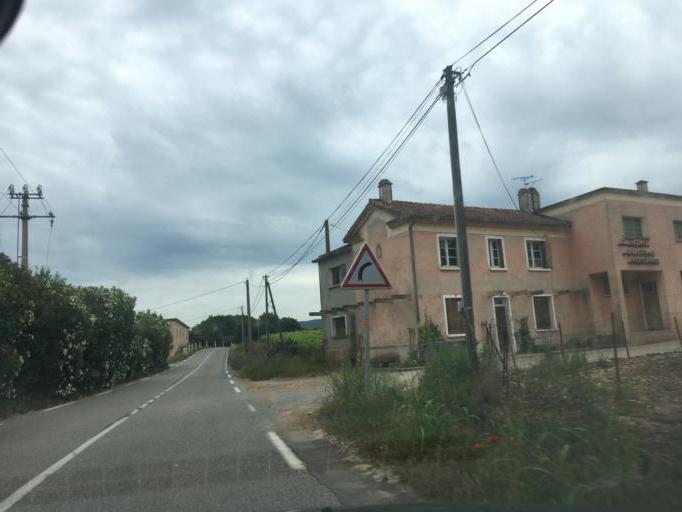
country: FR
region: Provence-Alpes-Cote d'Azur
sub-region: Departement du Var
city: Pierrefeu-du-Var
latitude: 43.2335
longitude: 6.1896
